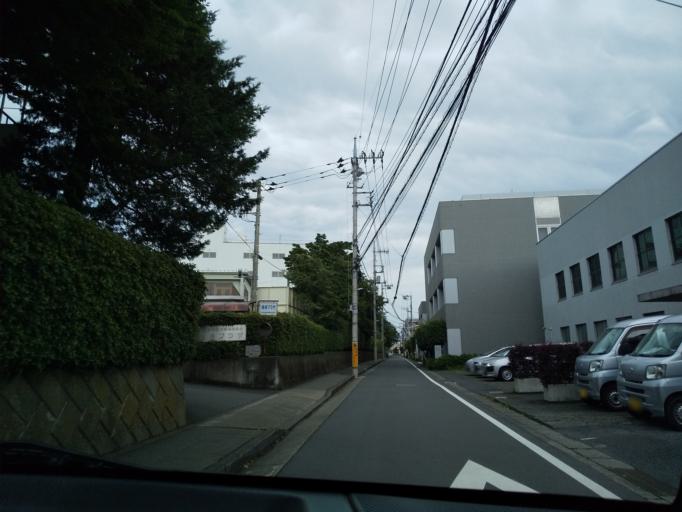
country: JP
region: Tokyo
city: Hino
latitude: 35.6757
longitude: 139.3836
